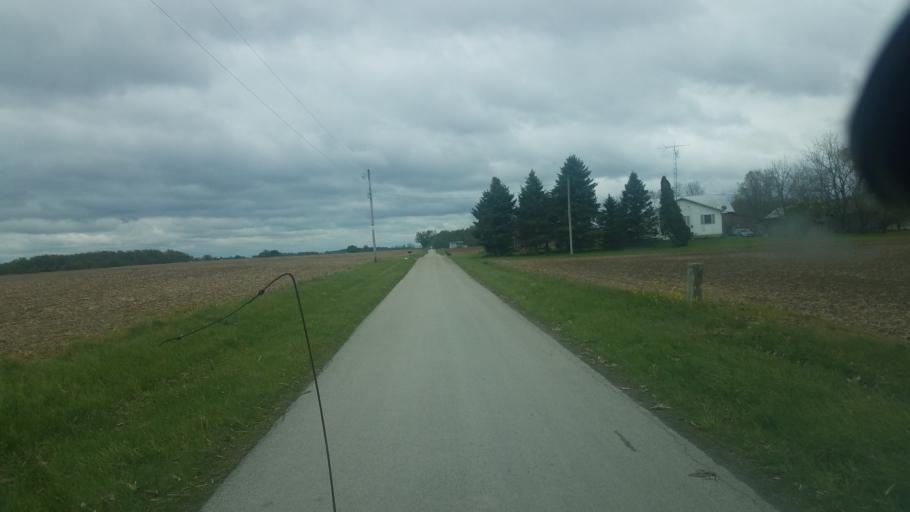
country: US
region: Ohio
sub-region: Wyandot County
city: Upper Sandusky
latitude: 40.7520
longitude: -83.1450
